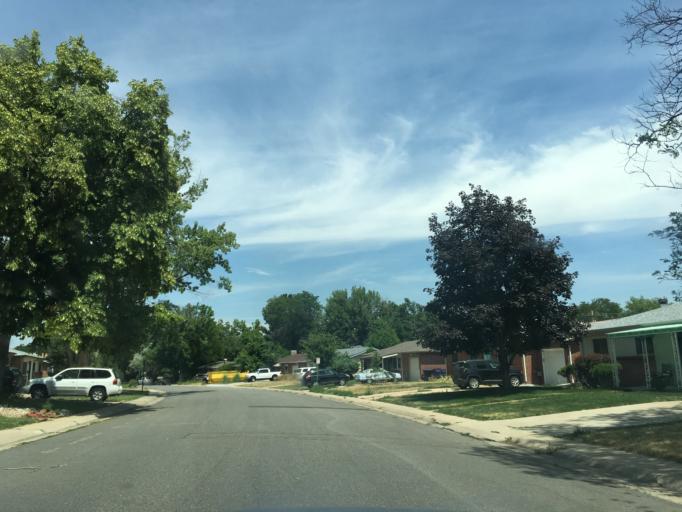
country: US
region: Colorado
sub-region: Arapahoe County
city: Sheridan
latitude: 39.6795
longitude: -105.0354
